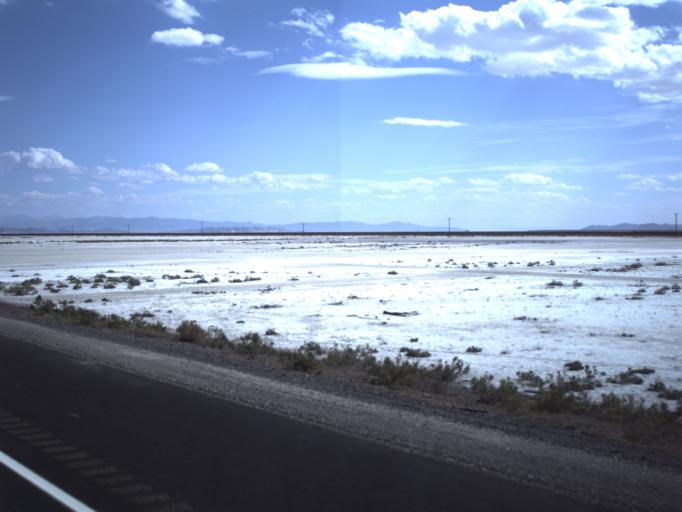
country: US
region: Utah
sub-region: Tooele County
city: Wendover
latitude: 40.7312
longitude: -113.5149
